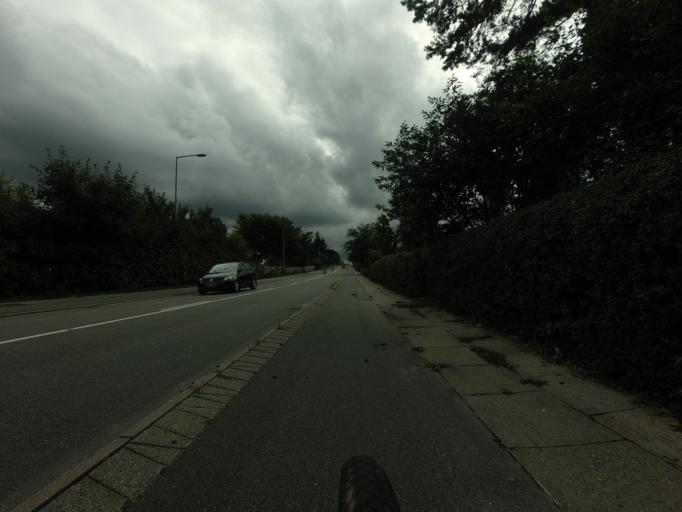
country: DK
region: North Denmark
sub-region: Hjorring Kommune
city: Hjorring
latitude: 57.4687
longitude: 9.9870
